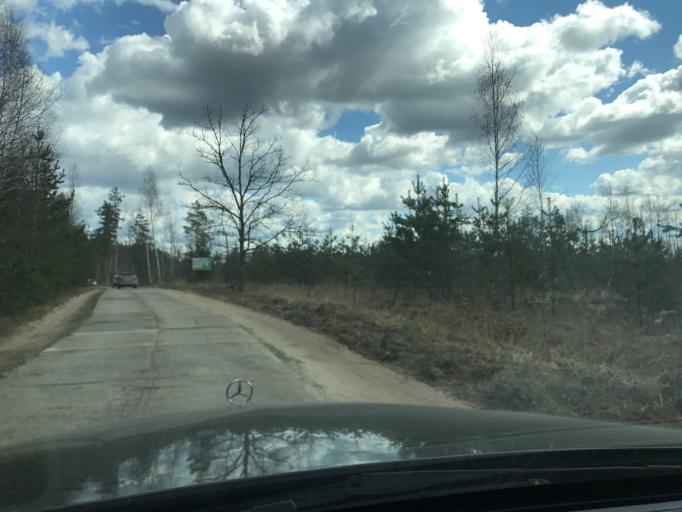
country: RU
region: Vladimir
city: Pokrov
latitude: 55.8432
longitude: 39.1411
